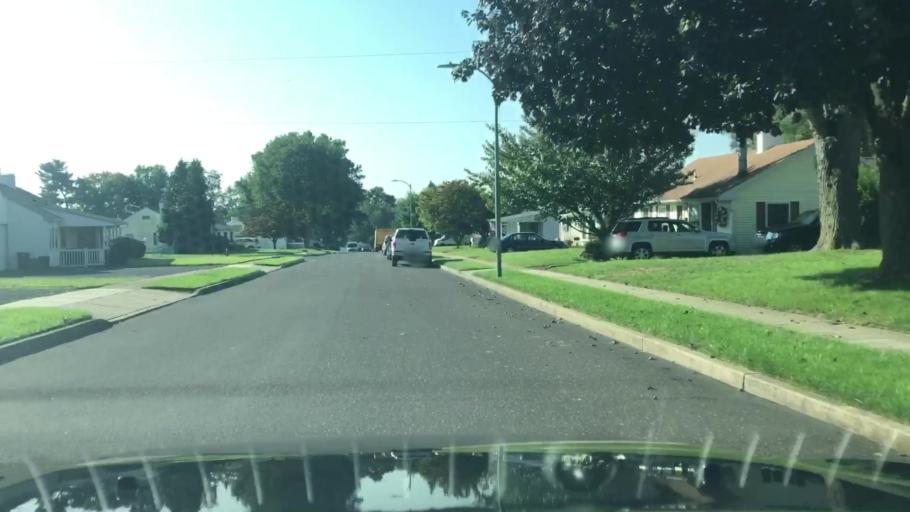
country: US
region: Pennsylvania
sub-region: Bucks County
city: Fairless Hills
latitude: 40.1797
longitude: -74.8615
